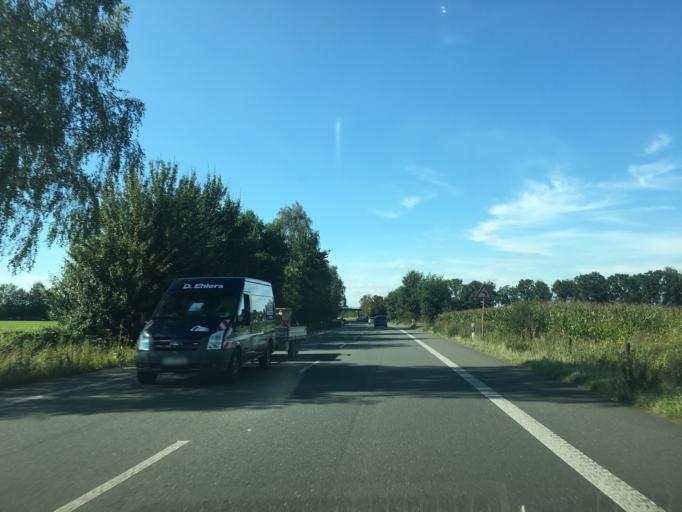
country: DE
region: North Rhine-Westphalia
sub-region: Regierungsbezirk Detmold
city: Rheda-Wiedenbruck
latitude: 51.8782
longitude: 8.2990
